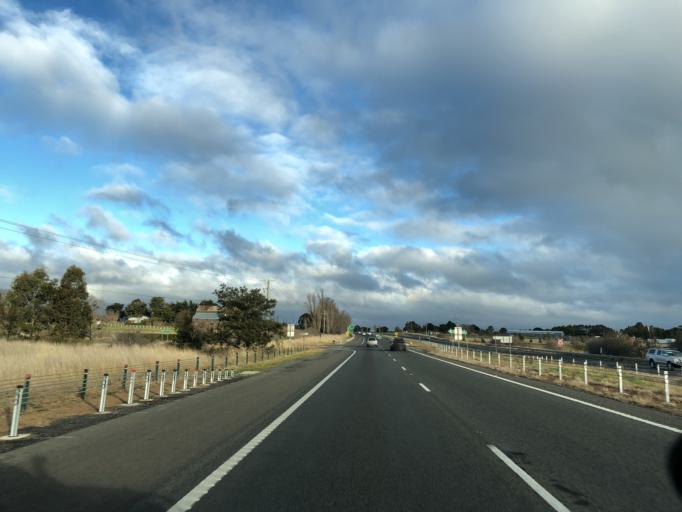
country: AU
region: Victoria
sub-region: Mount Alexander
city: Castlemaine
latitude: -37.2144
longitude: 144.4142
